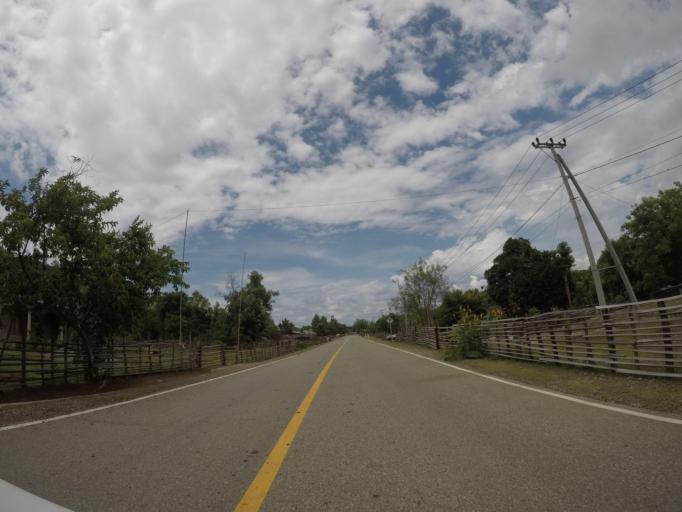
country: TL
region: Bobonaro
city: Maliana
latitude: -8.8389
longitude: 125.0588
